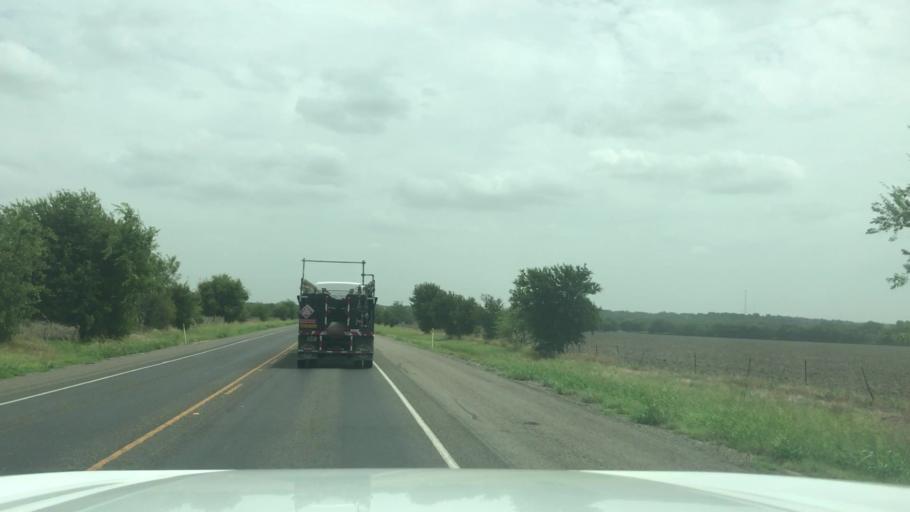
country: US
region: Texas
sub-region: Bosque County
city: Valley Mills
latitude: 31.6655
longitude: -97.4931
